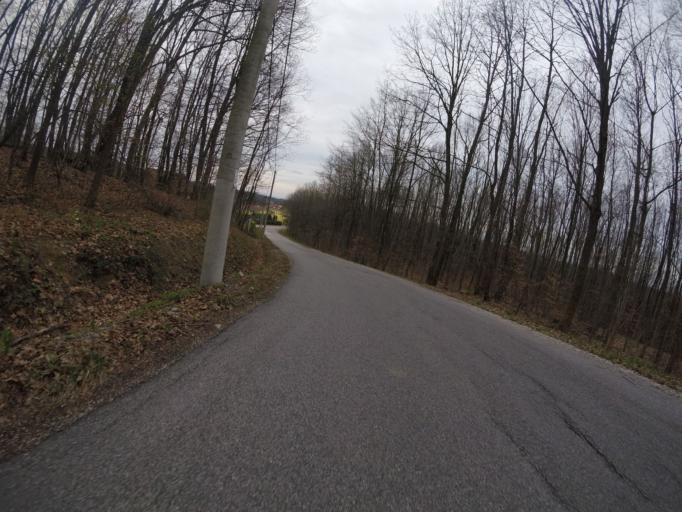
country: HR
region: Grad Zagreb
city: Strmec
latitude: 45.6330
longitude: 15.9358
